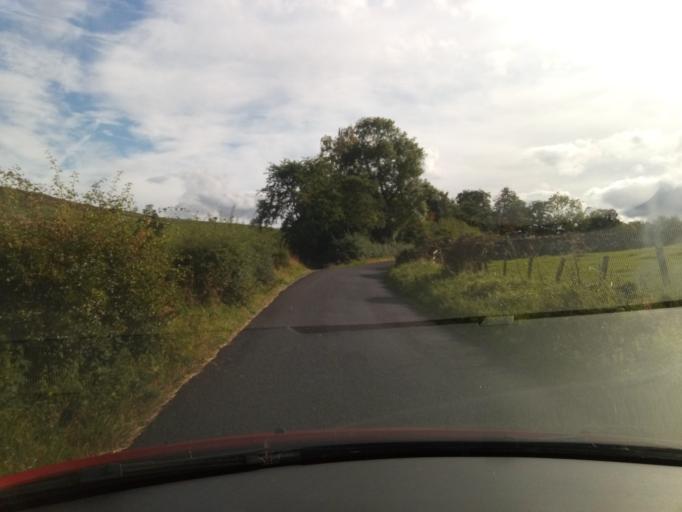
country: GB
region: Scotland
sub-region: The Scottish Borders
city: Kelso
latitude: 55.4871
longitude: -2.3479
